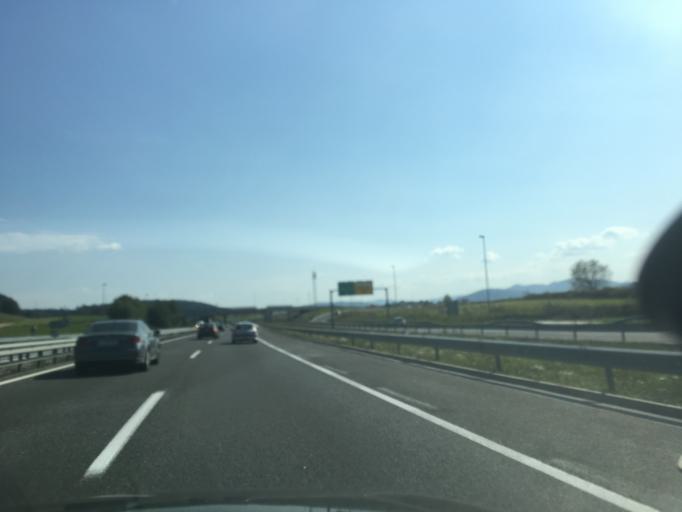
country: SI
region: Grosuplje
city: Smarje-Sap
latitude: 45.9730
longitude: 14.6271
